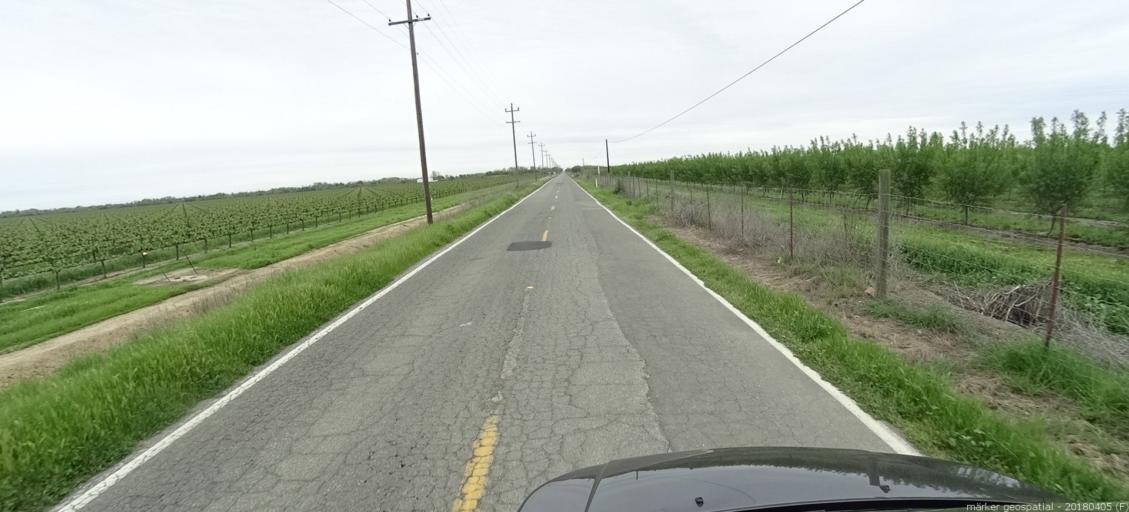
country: US
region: California
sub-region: Sacramento County
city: Walnut Grove
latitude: 38.3206
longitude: -121.5177
